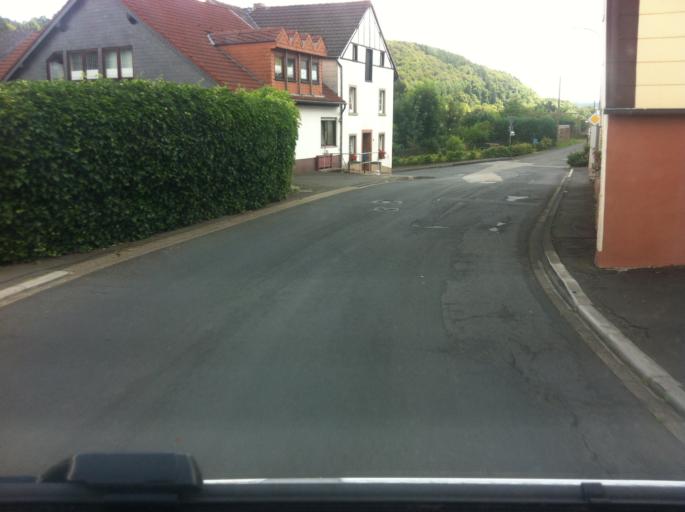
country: DE
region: Rheinland-Pfalz
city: Kalenborn-Scheuern
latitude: 50.2401
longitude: 6.6121
